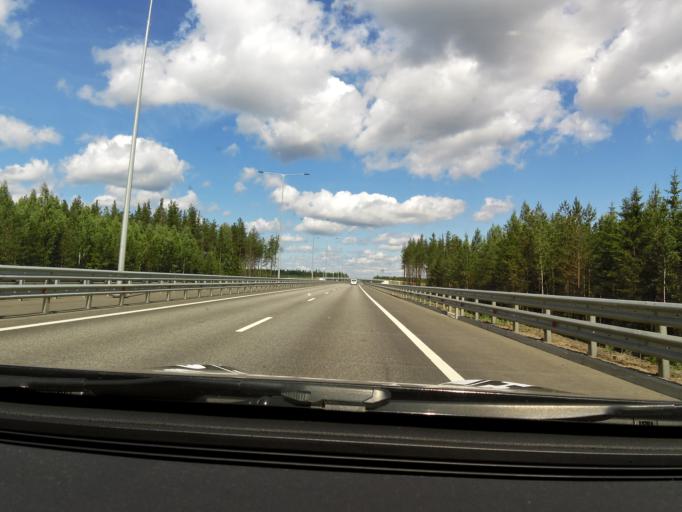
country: RU
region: Tverskaya
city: Krasnomayskiy
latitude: 57.5887
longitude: 34.2544
